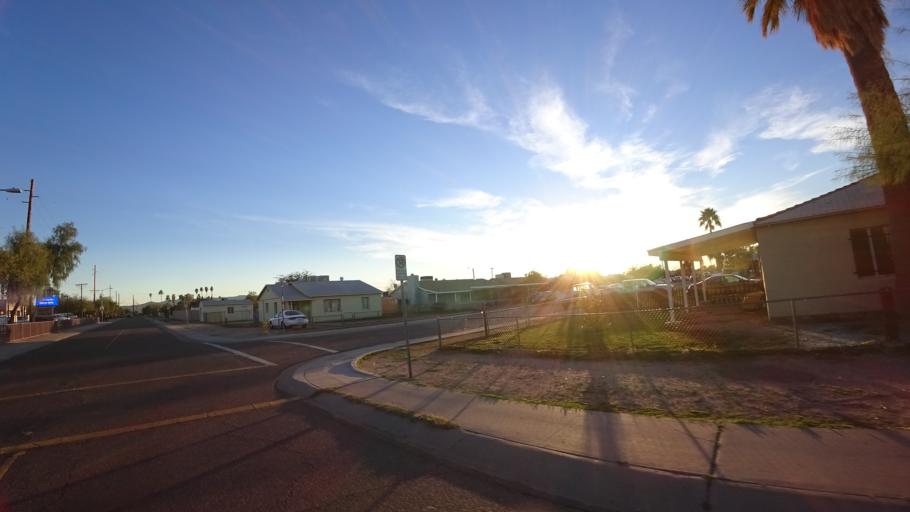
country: US
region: Arizona
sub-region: Maricopa County
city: Phoenix
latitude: 33.4552
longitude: -112.0042
